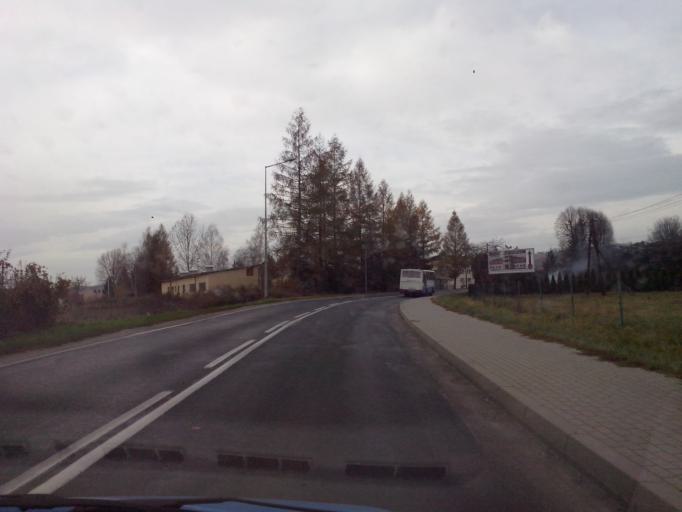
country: PL
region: Subcarpathian Voivodeship
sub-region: Powiat strzyzowski
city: Czudec
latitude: 49.9384
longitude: 21.8484
